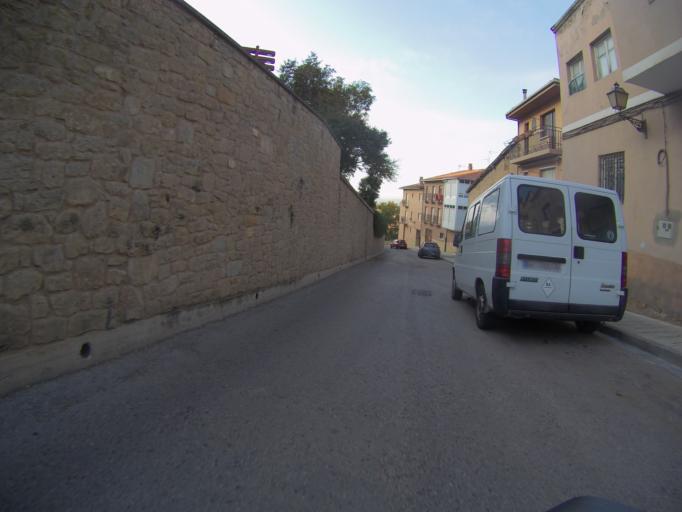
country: ES
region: Navarre
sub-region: Provincia de Navarra
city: Viana
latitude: 42.5154
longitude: -2.3746
